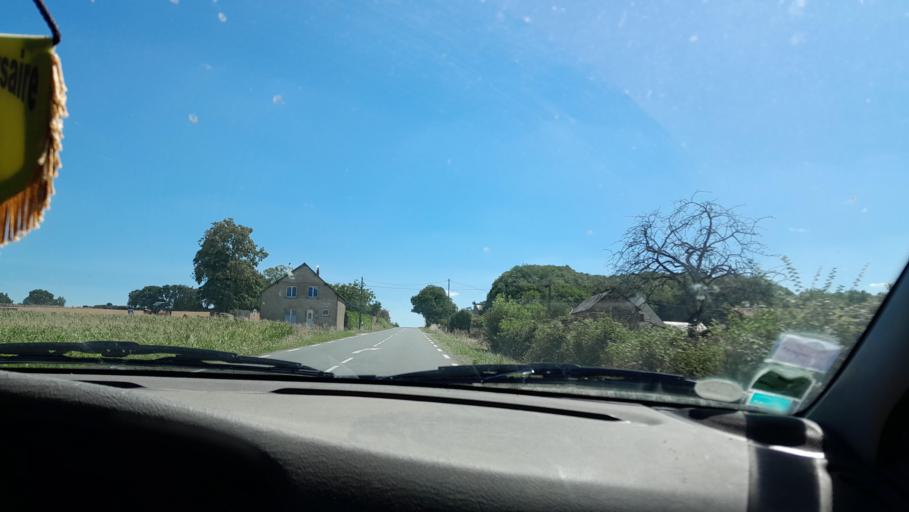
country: FR
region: Pays de la Loire
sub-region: Departement de la Loire-Atlantique
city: Saint-Mars-la-Jaille
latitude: 47.5472
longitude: -1.1861
